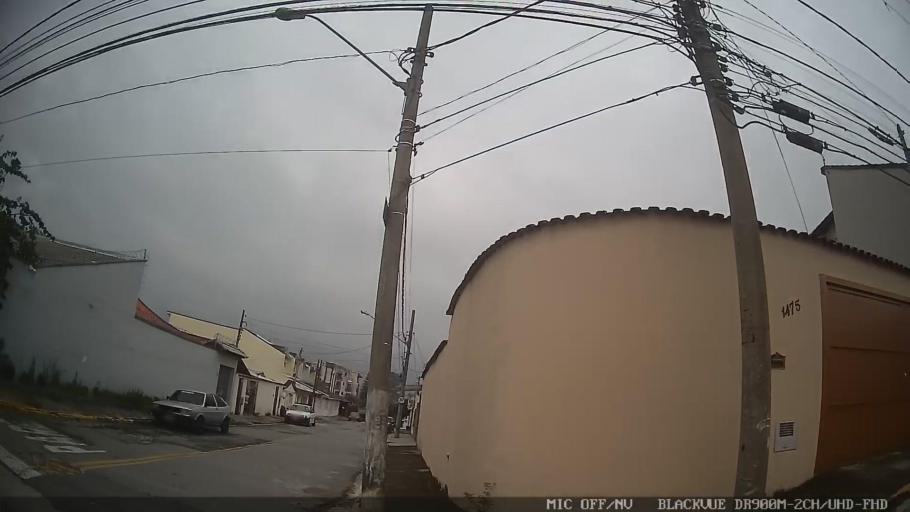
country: BR
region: Sao Paulo
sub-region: Mogi das Cruzes
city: Mogi das Cruzes
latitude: -23.5240
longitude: -46.1653
